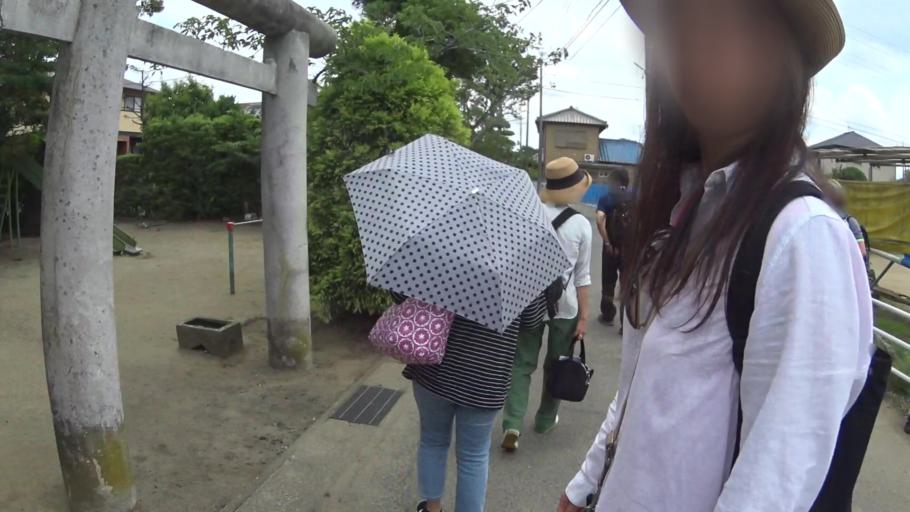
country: JP
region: Chiba
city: Katori-shi
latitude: 35.8993
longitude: 140.5316
